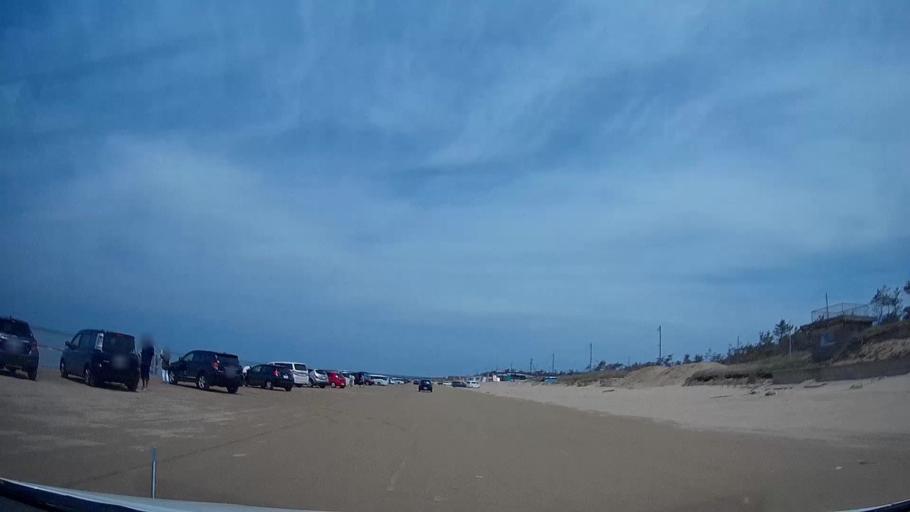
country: JP
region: Ishikawa
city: Hakui
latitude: 36.8401
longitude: 136.7494
